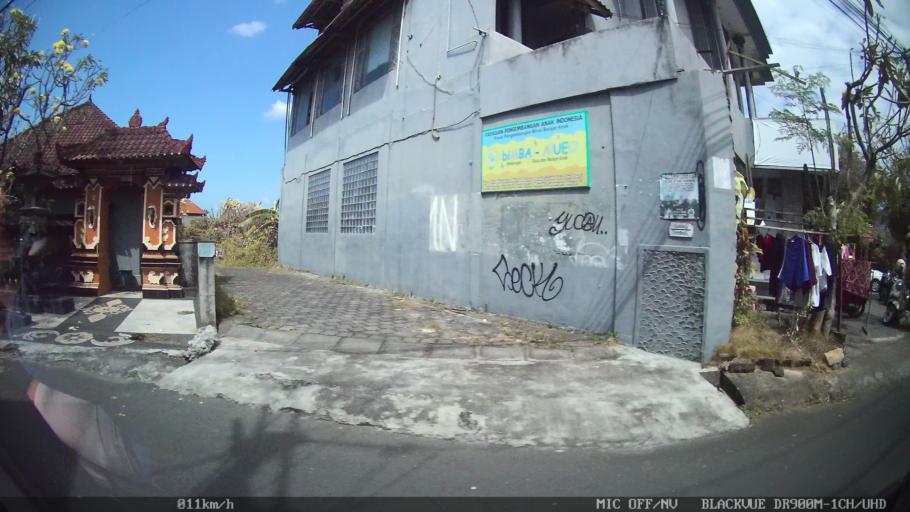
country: ID
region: Bali
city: Denpasar
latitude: -8.6769
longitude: 115.1836
